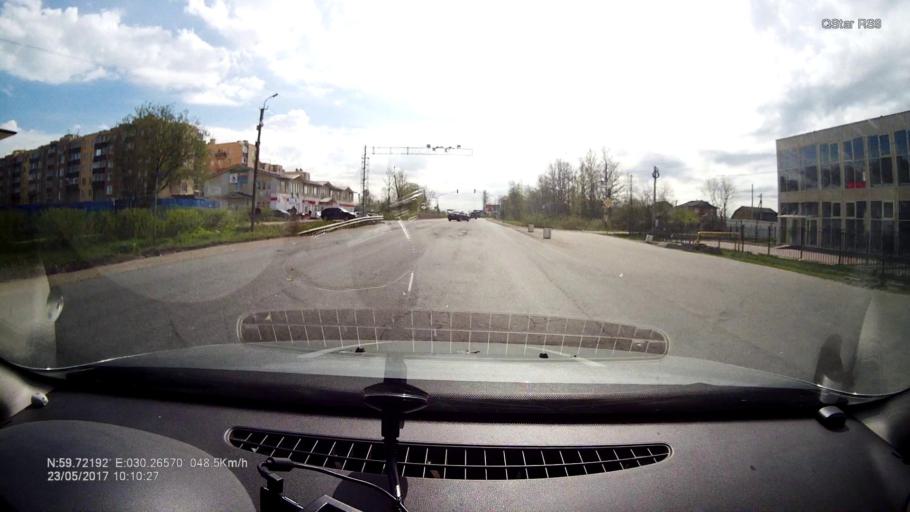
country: RU
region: St.-Petersburg
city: Aleksandrovskaya
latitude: 59.7219
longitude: 30.2658
